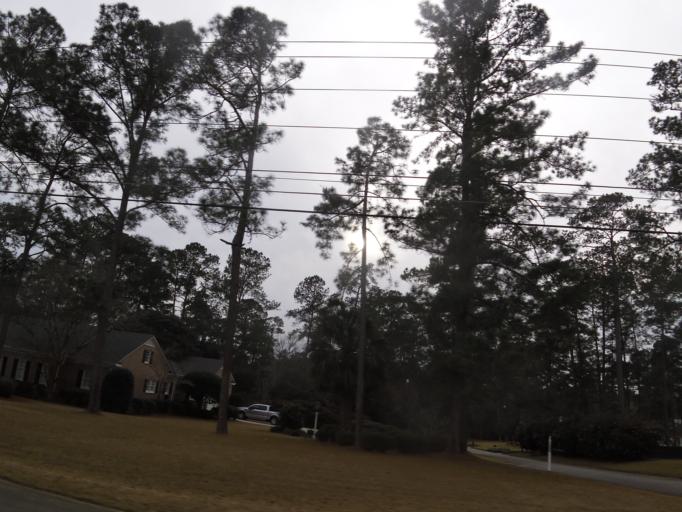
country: US
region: Georgia
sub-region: Thomas County
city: Thomasville
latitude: 30.8165
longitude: -83.9671
